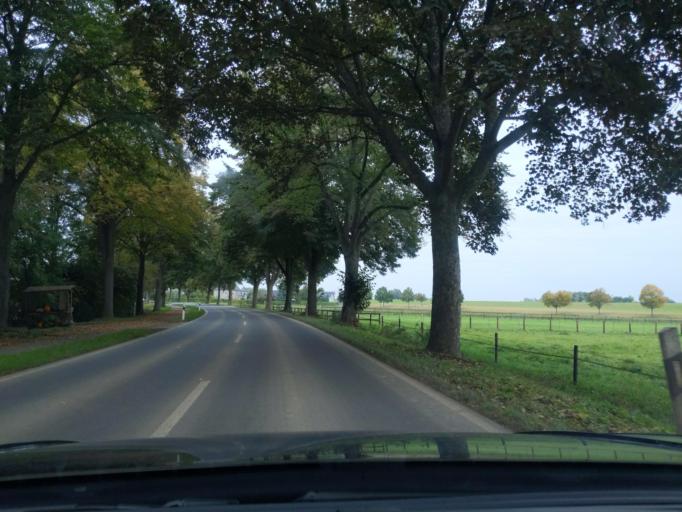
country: DE
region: North Rhine-Westphalia
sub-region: Regierungsbezirk Dusseldorf
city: Kleve
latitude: 51.8465
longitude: 6.0822
